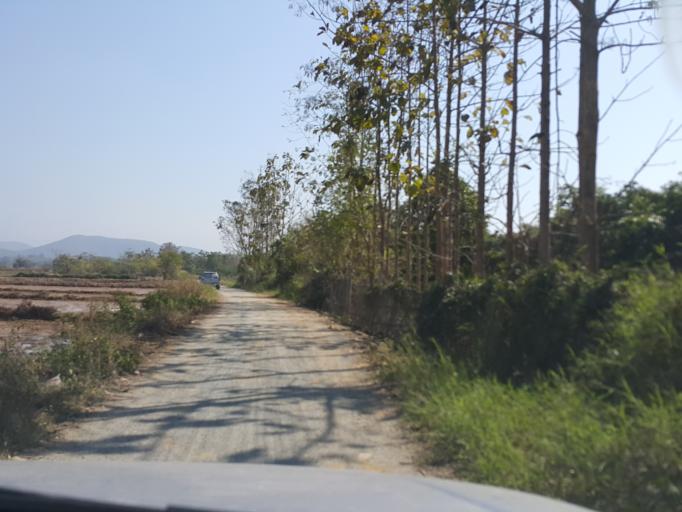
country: TH
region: Chiang Mai
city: San Sai
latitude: 18.8368
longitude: 99.1337
